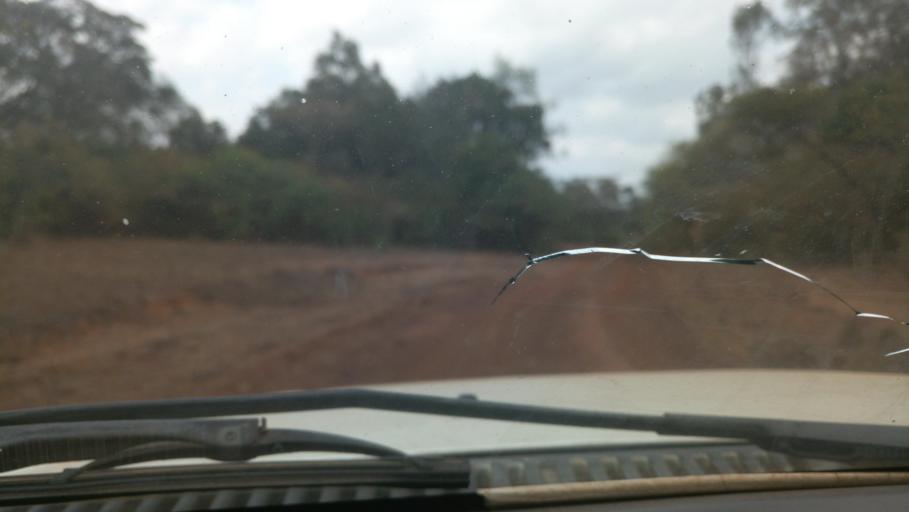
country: KE
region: Nairobi Area
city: Nairobi
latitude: -1.3635
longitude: 36.7846
